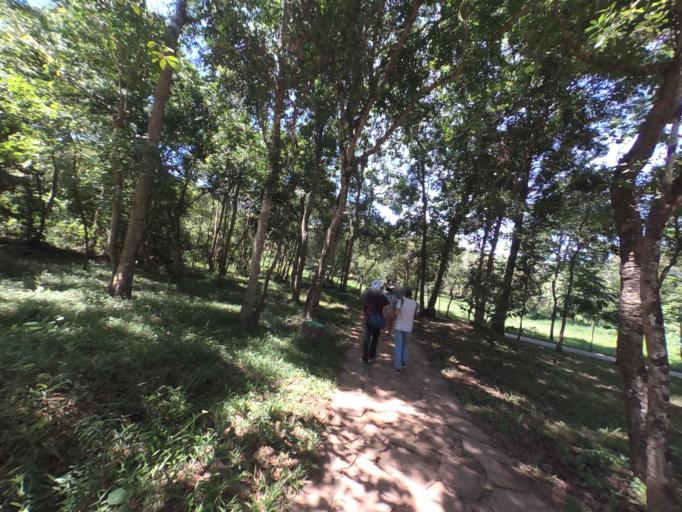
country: VN
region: Quang Nam
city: Dai Loc
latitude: 15.7643
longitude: 108.1252
